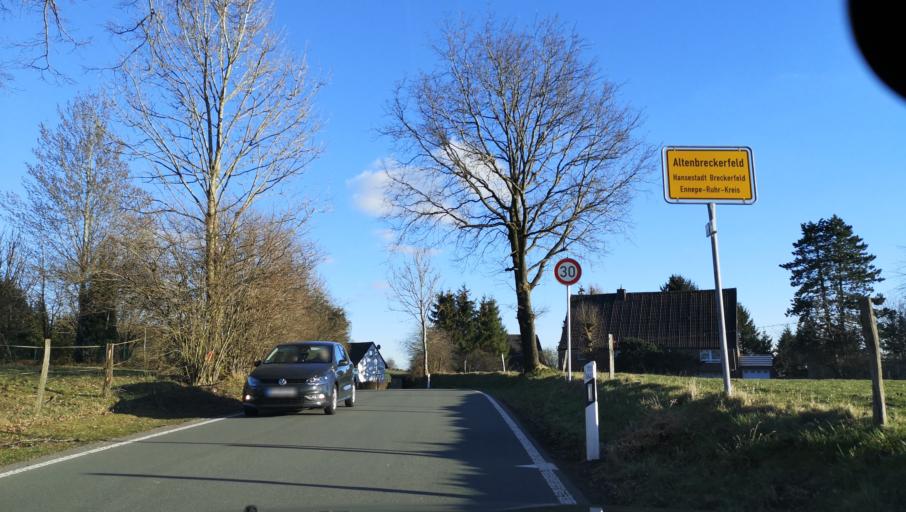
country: DE
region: North Rhine-Westphalia
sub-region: Regierungsbezirk Arnsberg
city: Breckerfeld
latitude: 51.2456
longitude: 7.4559
